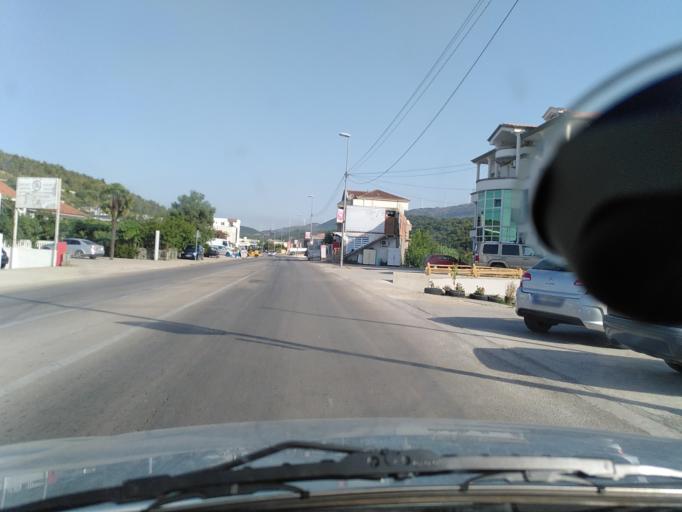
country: ME
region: Ulcinj
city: Ulcinj
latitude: 41.9340
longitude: 19.2225
